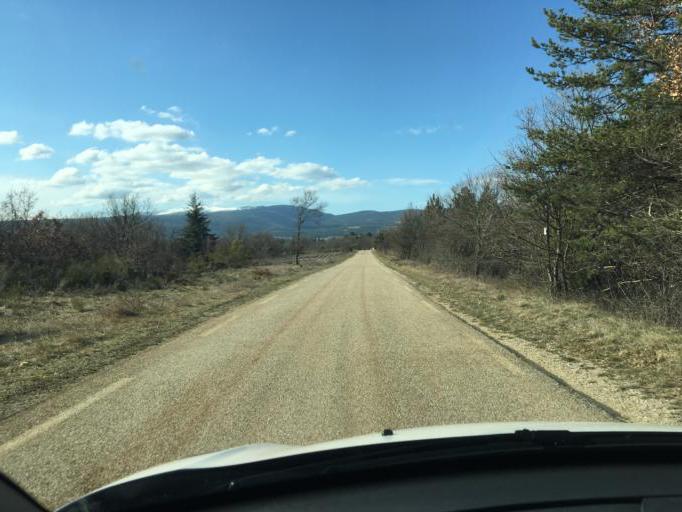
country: FR
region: Provence-Alpes-Cote d'Azur
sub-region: Departement du Vaucluse
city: Sault
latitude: 44.0777
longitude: 5.4189
